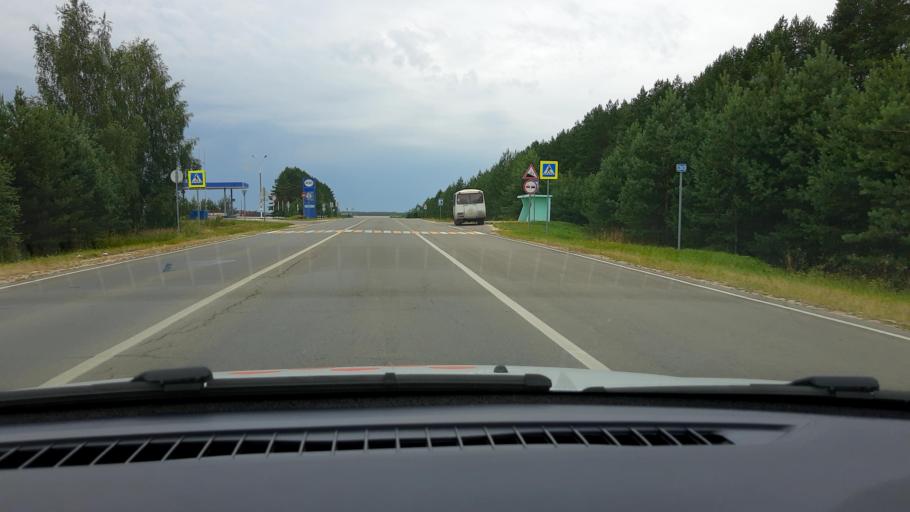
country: RU
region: Nizjnij Novgorod
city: Vyyezdnoye
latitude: 55.1508
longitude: 43.5695
